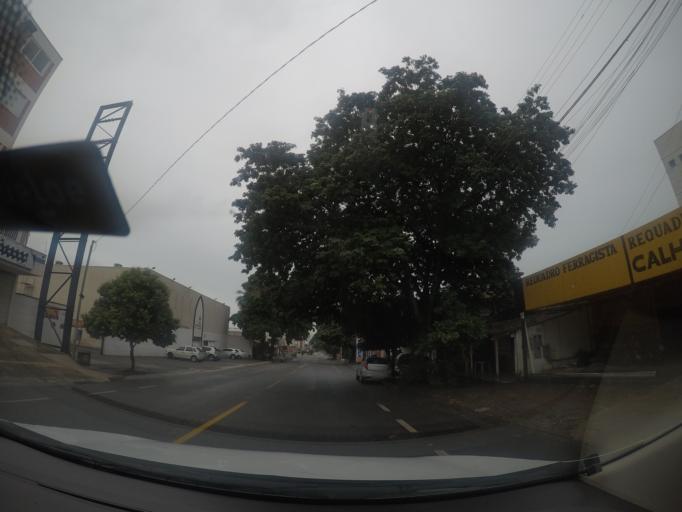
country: BR
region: Goias
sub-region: Goiania
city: Goiania
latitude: -16.7103
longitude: -49.2837
